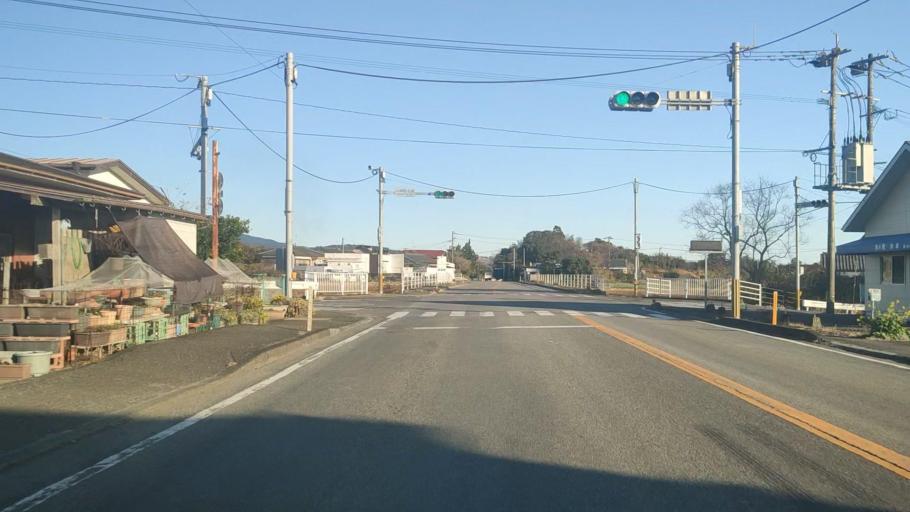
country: JP
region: Miyazaki
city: Takanabe
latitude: 32.2319
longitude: 131.5484
